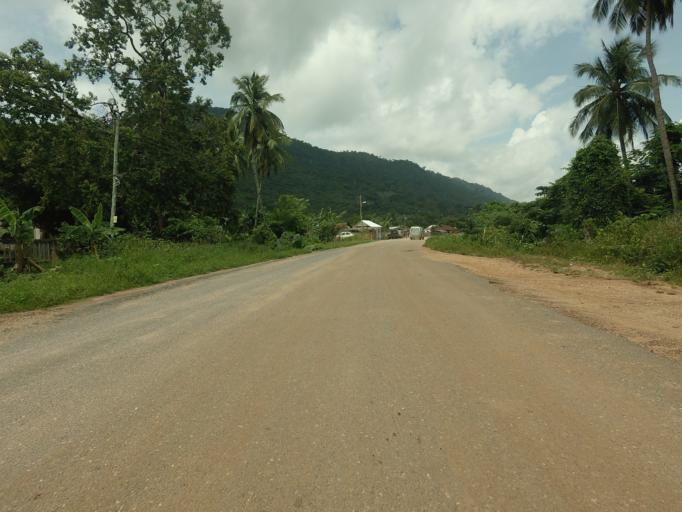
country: GH
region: Volta
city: Ho
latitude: 6.7645
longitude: 0.3642
